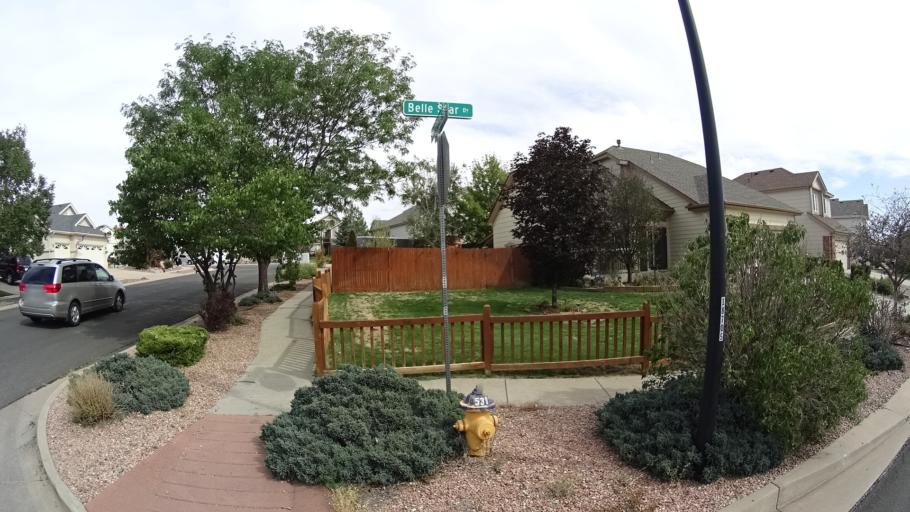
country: US
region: Colorado
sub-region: El Paso County
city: Cimarron Hills
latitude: 38.9103
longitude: -104.6992
